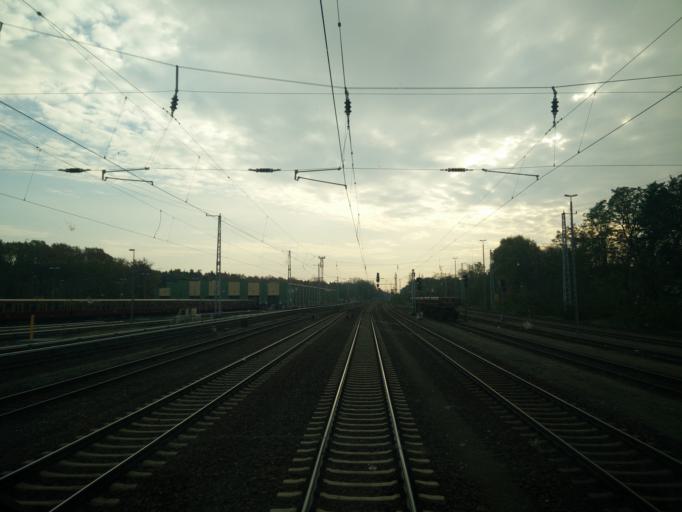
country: DE
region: Berlin
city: Grunau
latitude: 52.4067
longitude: 13.5822
